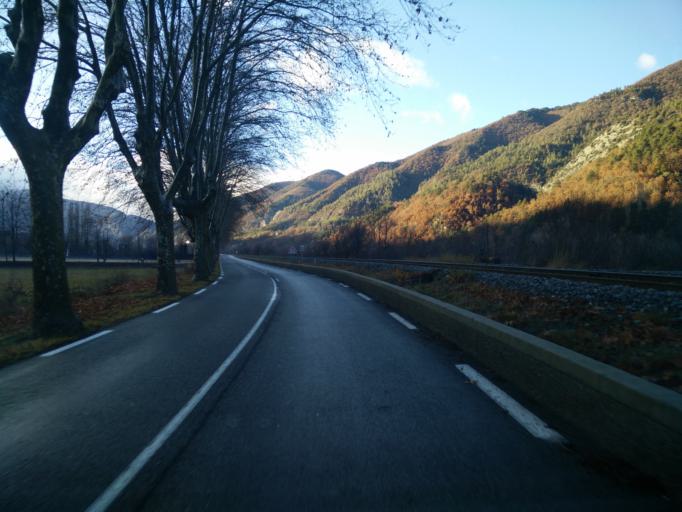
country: FR
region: Provence-Alpes-Cote d'Azur
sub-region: Departement des Alpes-Maritimes
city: Puget-Theniers
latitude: 43.9533
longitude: 6.8694
